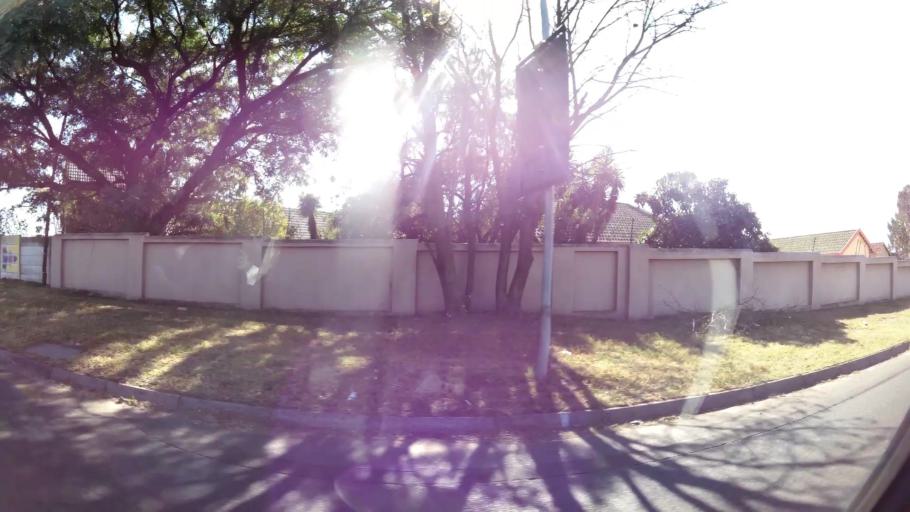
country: ZA
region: Gauteng
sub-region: City of Johannesburg Metropolitan Municipality
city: Roodepoort
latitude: -26.1169
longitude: 27.8516
